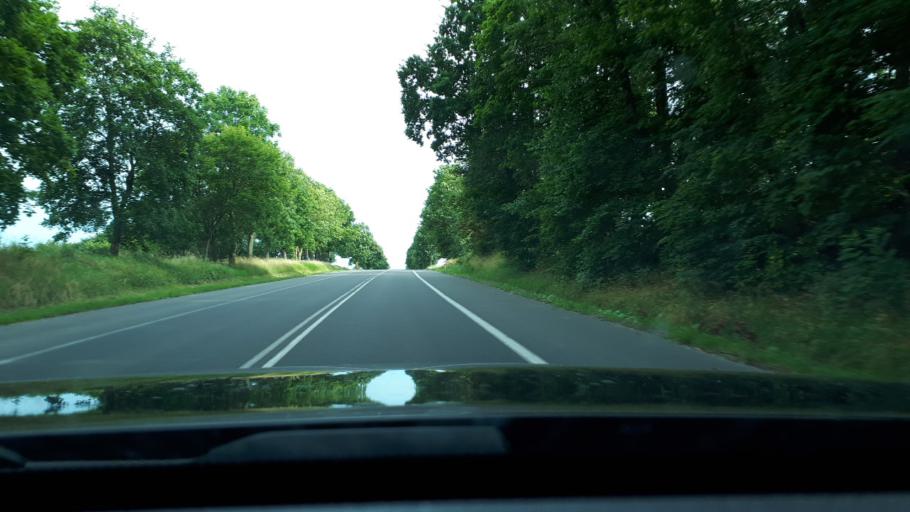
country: PL
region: Warmian-Masurian Voivodeship
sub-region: Powiat ostrodzki
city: Ostroda
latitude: 53.6429
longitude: 20.0538
